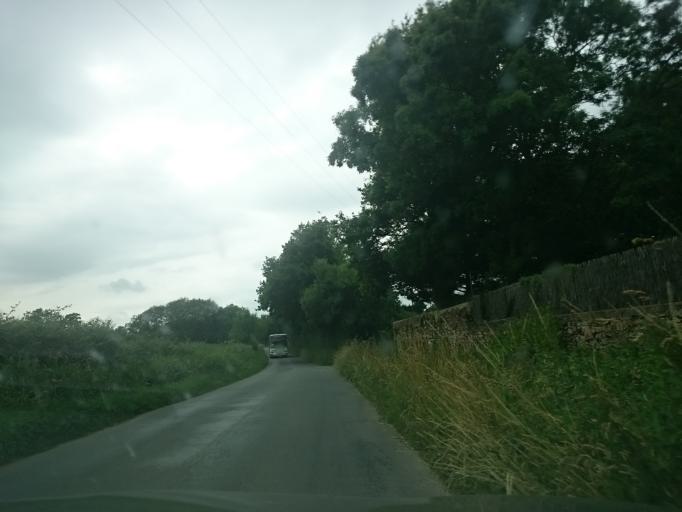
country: FR
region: Pays de la Loire
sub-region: Departement de la Loire-Atlantique
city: Le Pellerin
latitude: 47.2033
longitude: -1.7823
